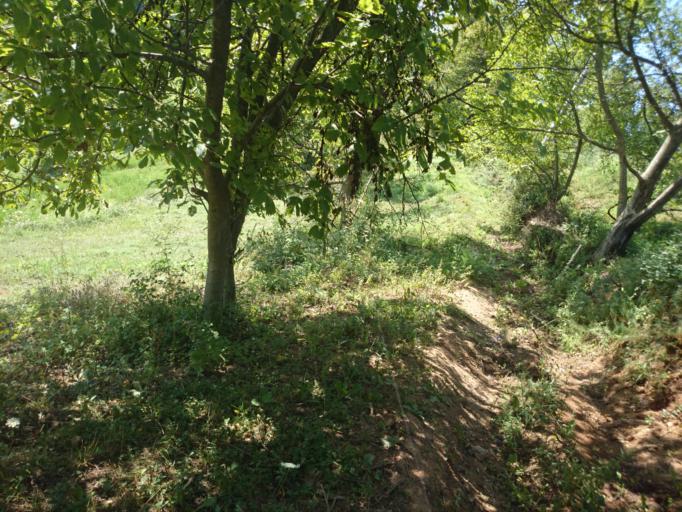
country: AL
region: Diber
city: Peshkopi
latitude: 41.6339
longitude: 20.4078
